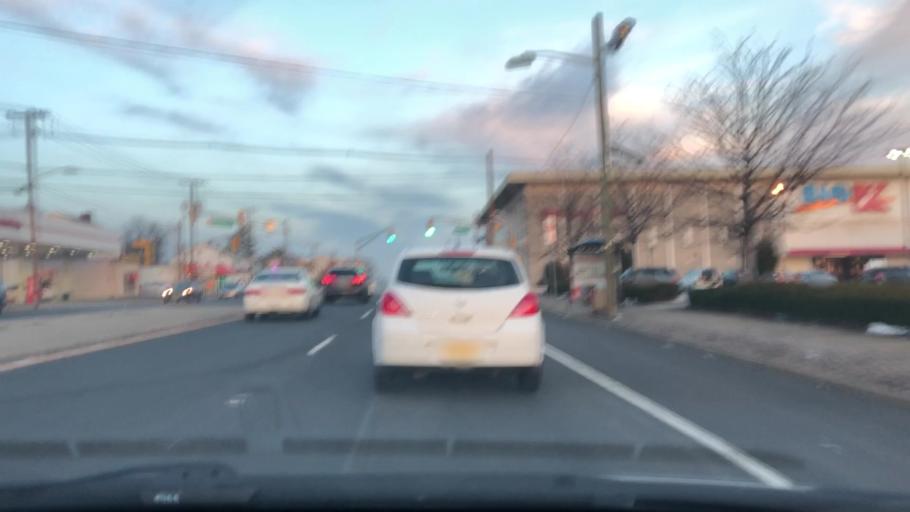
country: US
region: New Jersey
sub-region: Bergen County
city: Elmwood Park
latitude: 40.9196
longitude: -74.1235
